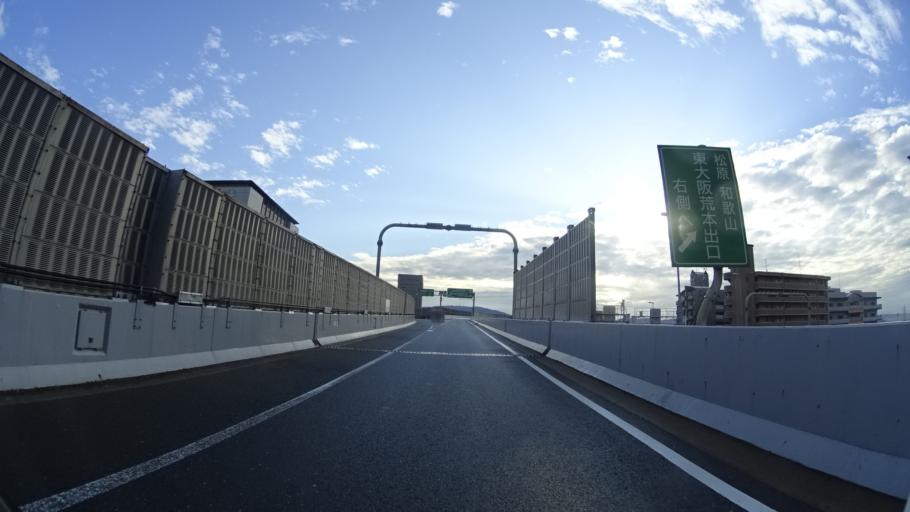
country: JP
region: Osaka
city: Daitocho
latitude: 34.6788
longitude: 135.5930
